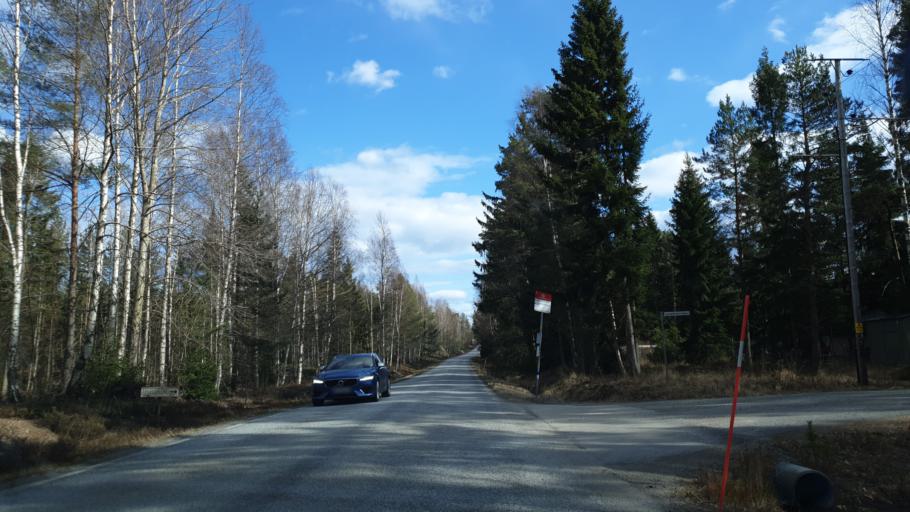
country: SE
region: Stockholm
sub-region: Varmdo Kommun
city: Mortnas
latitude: 59.2460
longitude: 18.4635
